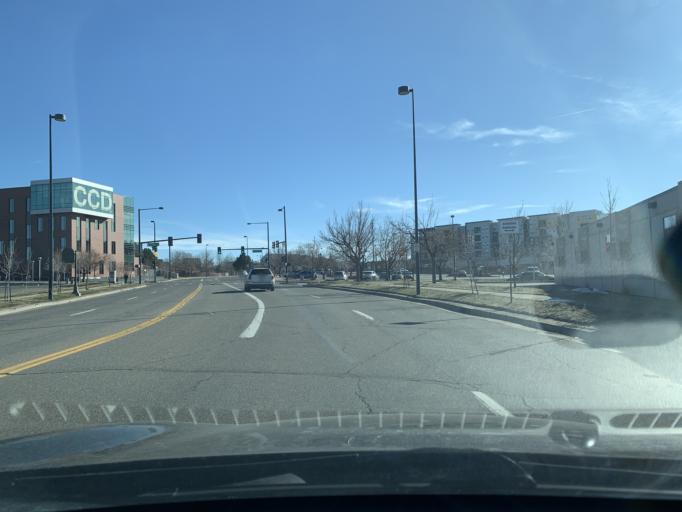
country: US
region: Colorado
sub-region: Denver County
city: Denver
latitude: 39.7417
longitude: -105.0070
